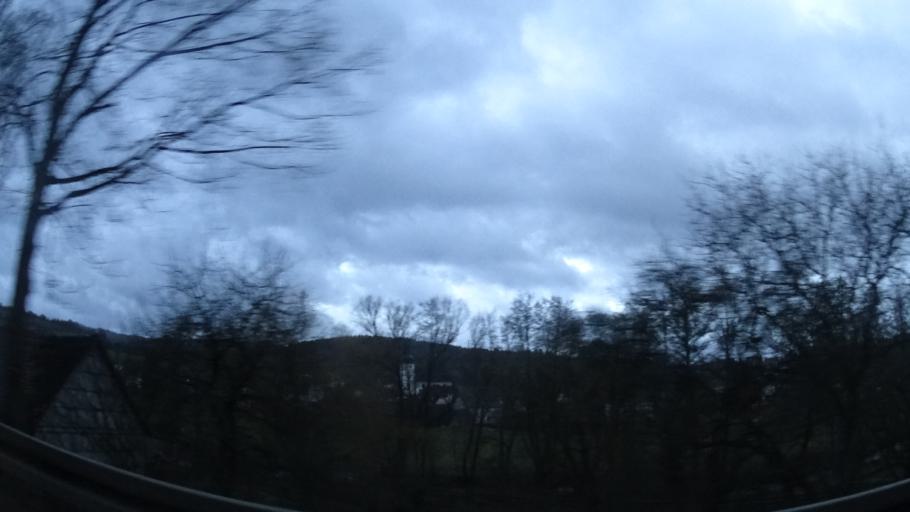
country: DE
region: Bavaria
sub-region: Regierungsbezirk Unterfranken
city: Motten
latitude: 50.4543
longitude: 9.7948
